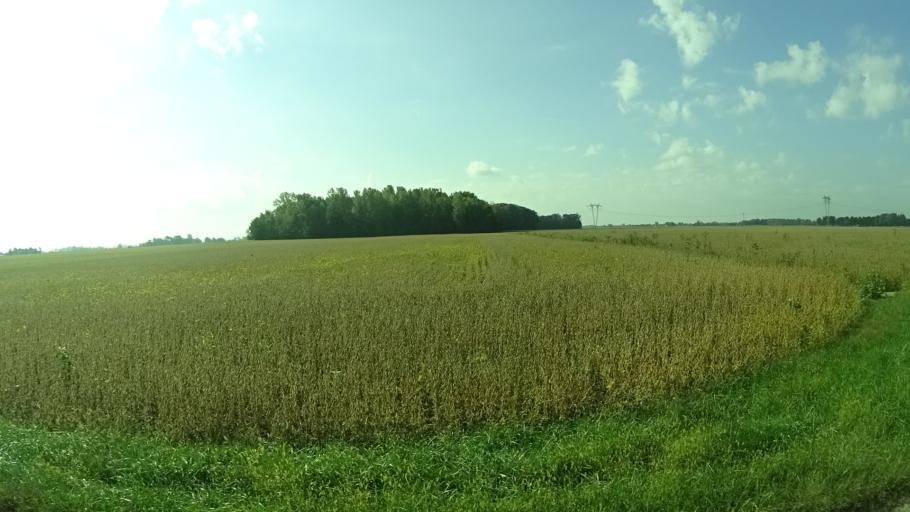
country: US
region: Indiana
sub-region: Madison County
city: Lapel
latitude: 40.0454
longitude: -85.8527
